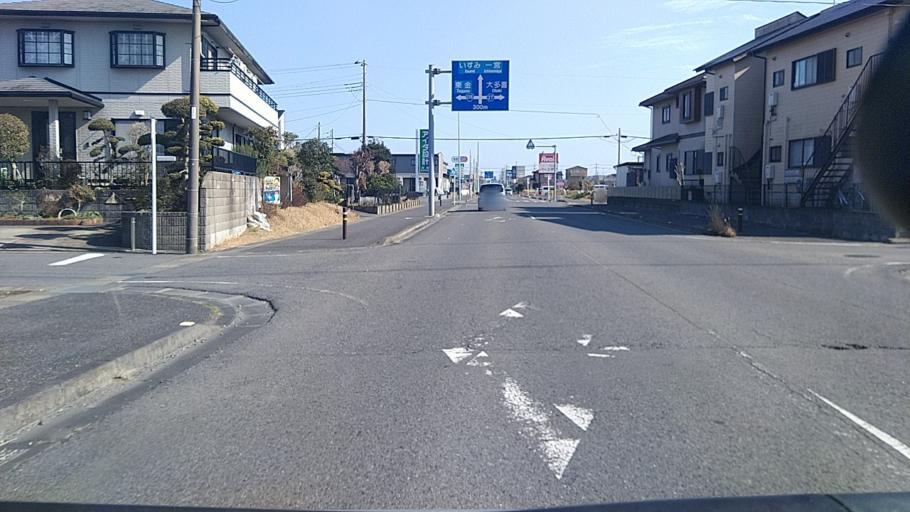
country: JP
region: Chiba
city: Mobara
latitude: 35.4248
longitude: 140.2840
